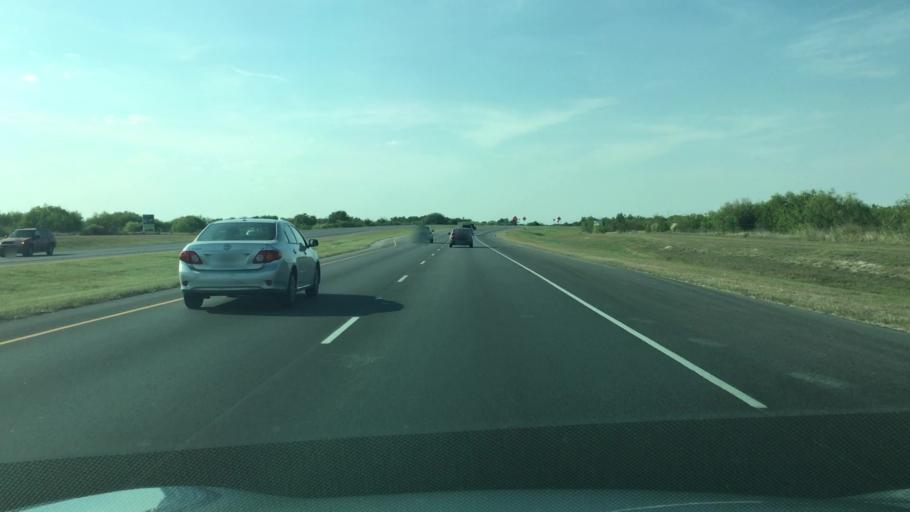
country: US
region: Texas
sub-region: Hays County
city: Kyle
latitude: 30.0417
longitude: -97.8738
